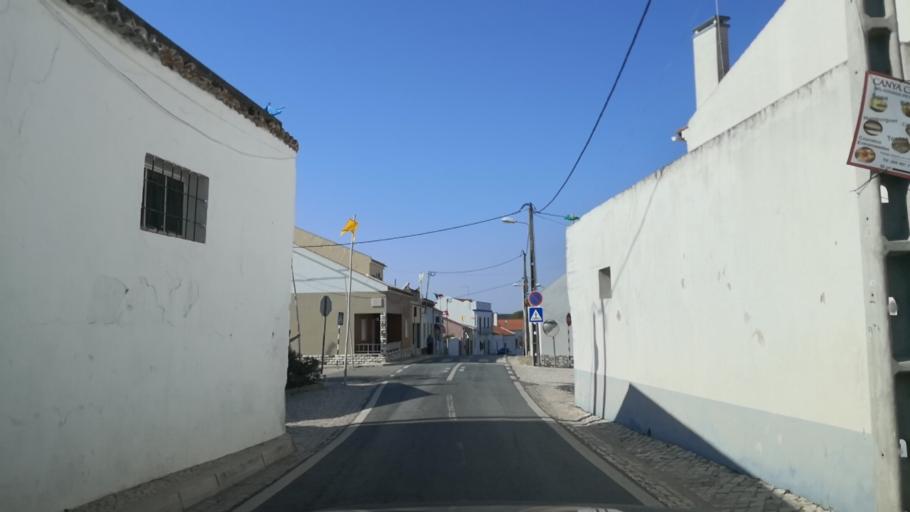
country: PT
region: Santarem
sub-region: Benavente
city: Poceirao
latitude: 38.7671
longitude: -8.6263
